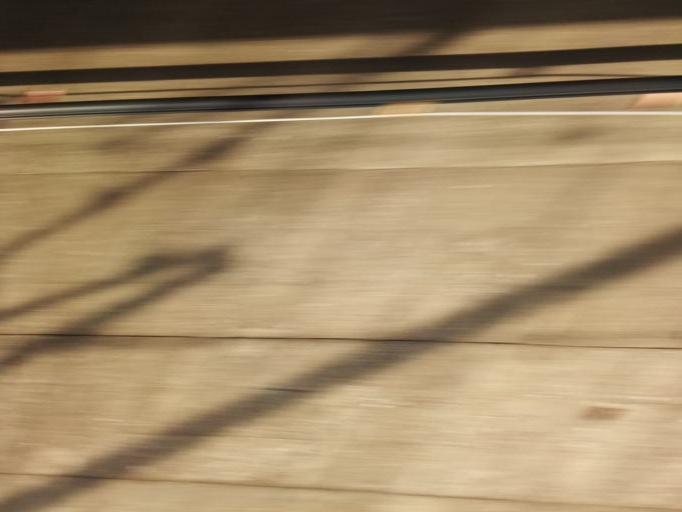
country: JP
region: Aichi
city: Gamagori
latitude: 34.8170
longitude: 137.2595
